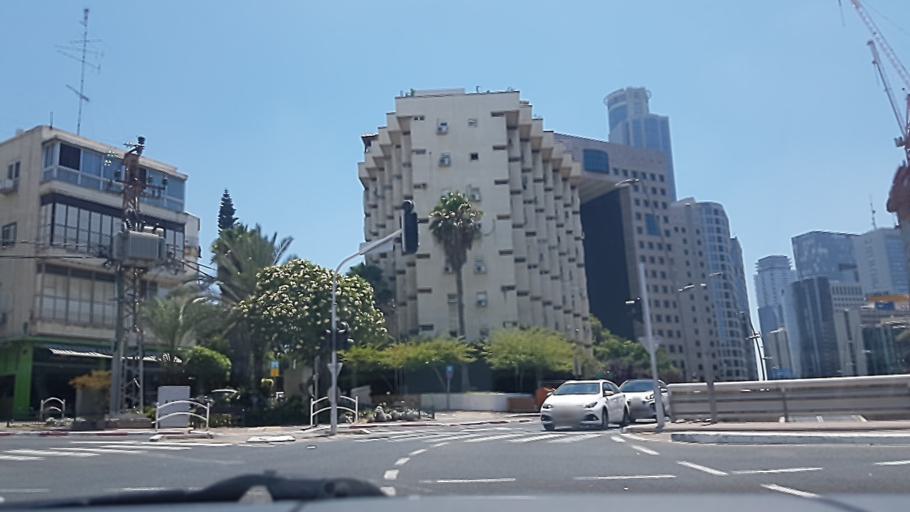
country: IL
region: Tel Aviv
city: Ramat Gan
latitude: 32.0876
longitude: 34.8062
